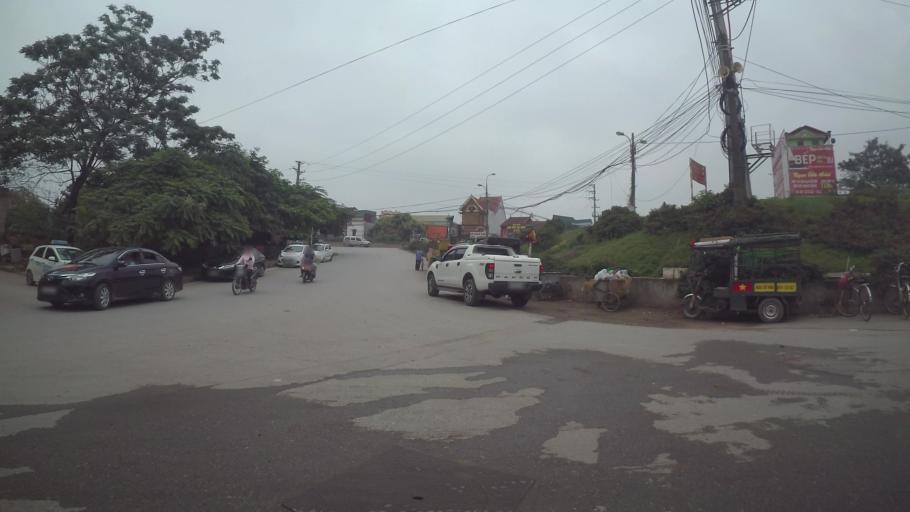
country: VN
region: Ha Noi
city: Hai BaTrung
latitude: 20.9930
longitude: 105.8919
